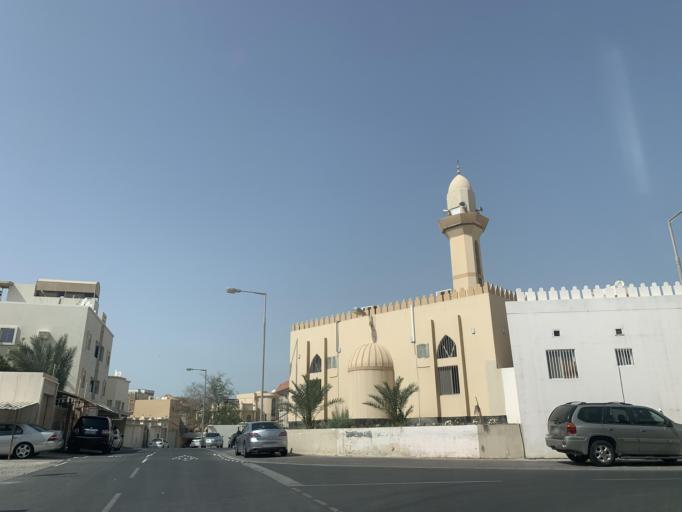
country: BH
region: Northern
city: Ar Rifa'
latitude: 26.1453
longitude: 50.5675
